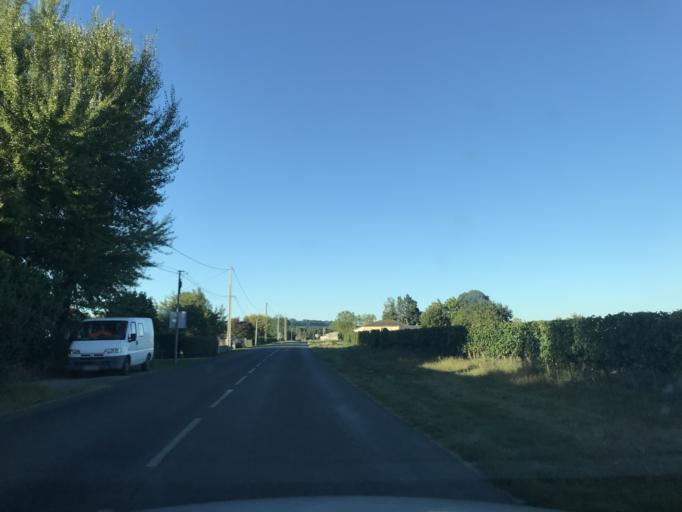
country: FR
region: Aquitaine
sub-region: Departement de la Gironde
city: Mouliets-et-Villemartin
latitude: 44.8369
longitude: -0.0388
